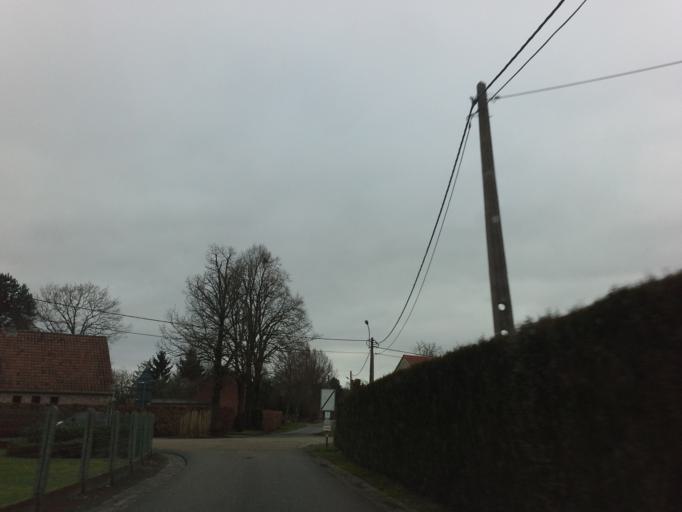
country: BE
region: Flanders
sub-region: Provincie Antwerpen
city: Meerhout
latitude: 51.1299
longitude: 5.0525
